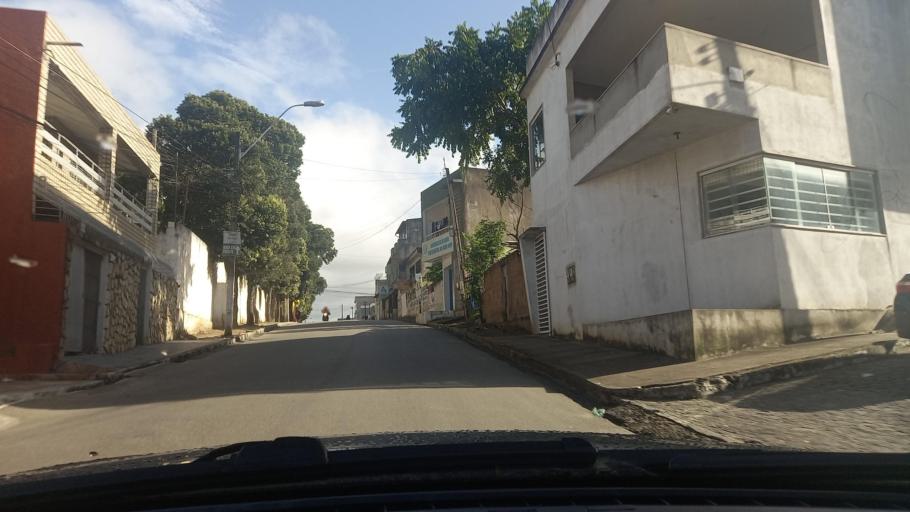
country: BR
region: Pernambuco
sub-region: Vitoria De Santo Antao
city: Vitoria de Santo Antao
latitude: -8.1130
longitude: -35.2967
